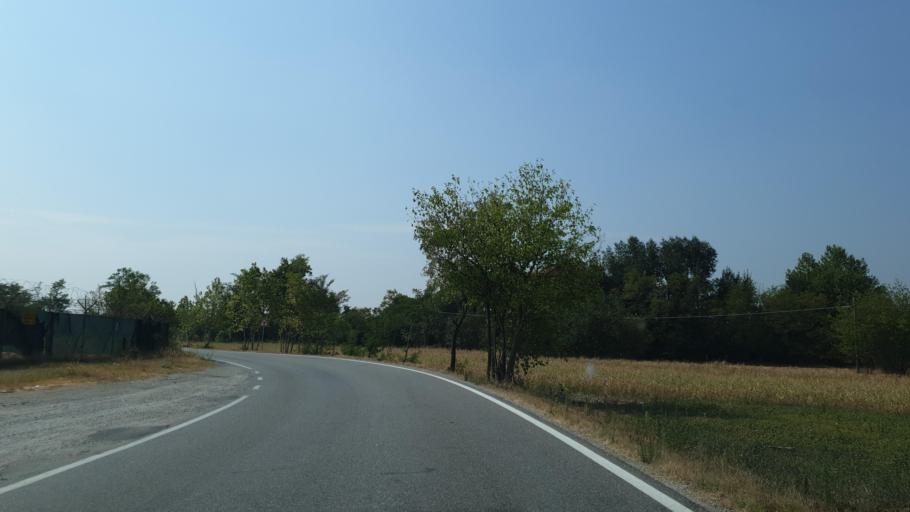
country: IT
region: Lombardy
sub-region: Provincia di Brescia
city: Montirone
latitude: 45.4427
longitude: 10.2524
